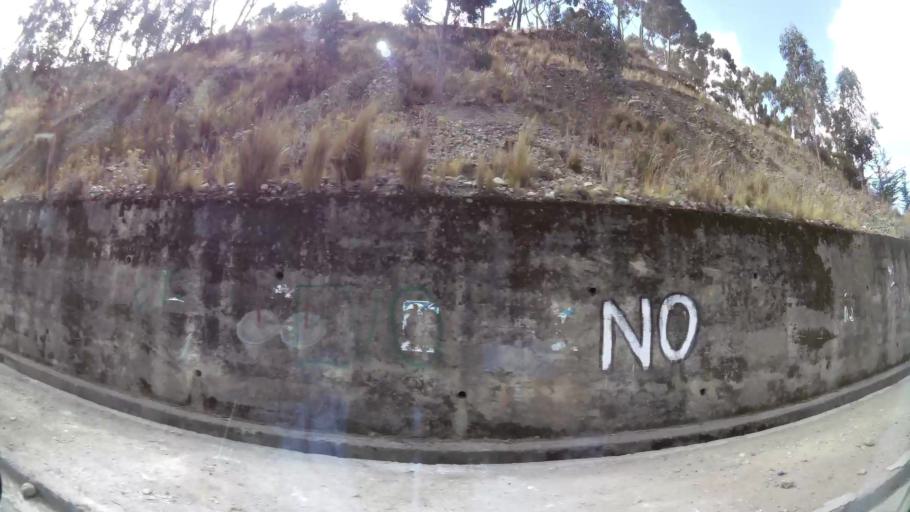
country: BO
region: La Paz
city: La Paz
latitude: -16.4640
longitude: -68.1115
